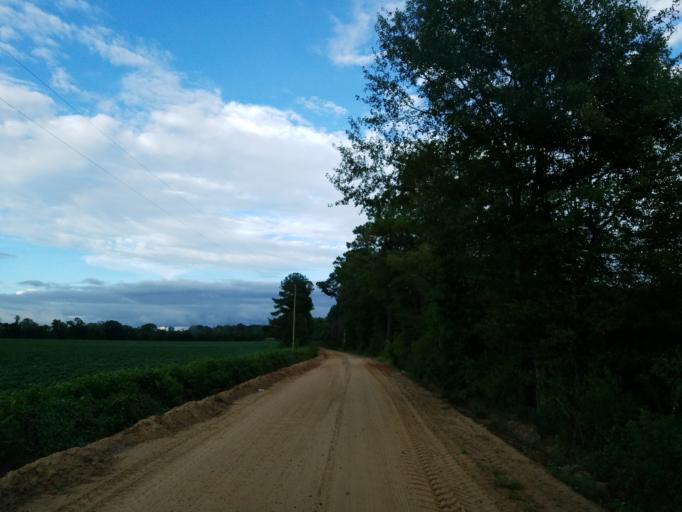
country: US
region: Georgia
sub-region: Cook County
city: Sparks
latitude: 31.2354
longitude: -83.4457
